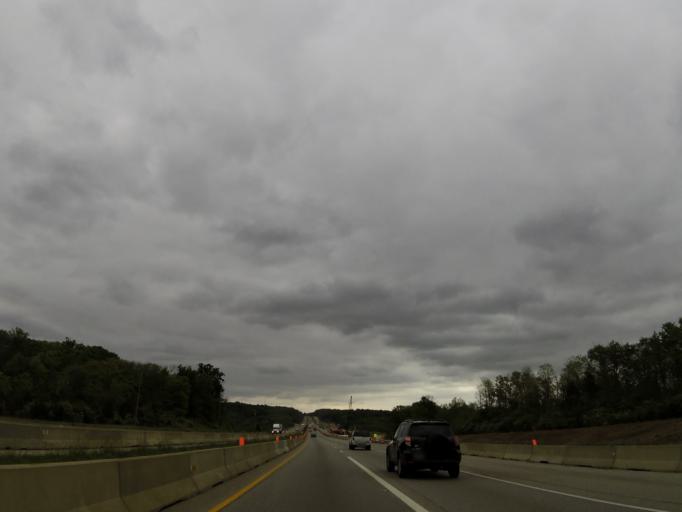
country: US
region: Ohio
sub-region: Warren County
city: Morrow
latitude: 39.4169
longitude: -84.1113
